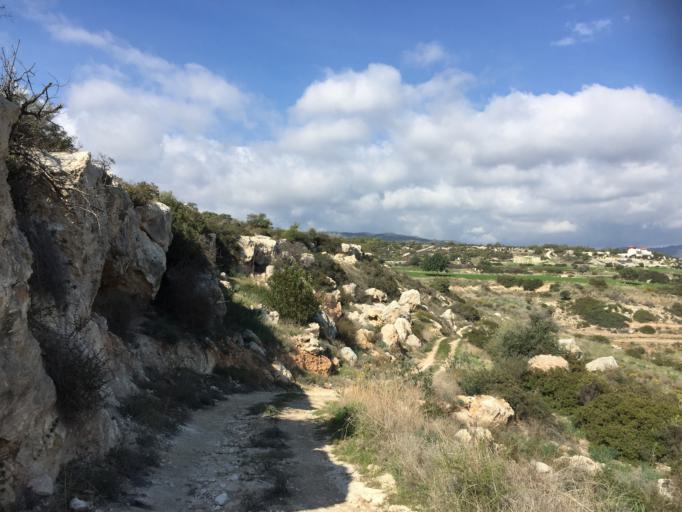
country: CY
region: Larnaka
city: Agios Tychon
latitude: 34.7376
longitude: 33.1418
